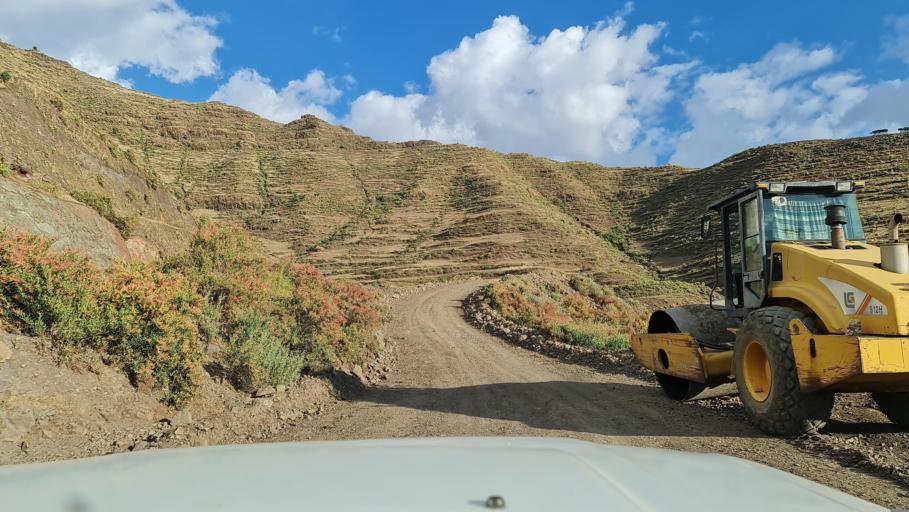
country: ET
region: Amhara
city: Debark'
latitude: 13.0499
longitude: 38.0199
